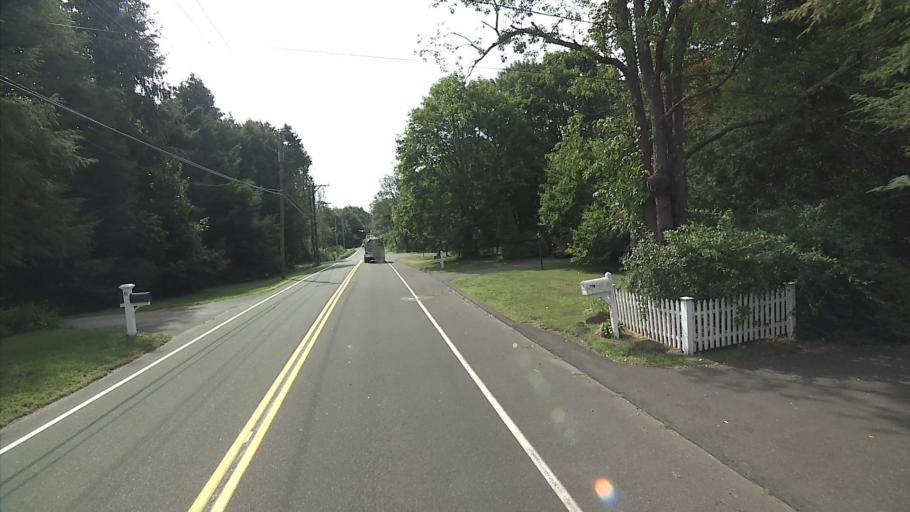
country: US
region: Connecticut
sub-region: New Haven County
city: Woodbridge
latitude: 41.3352
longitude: -73.0012
